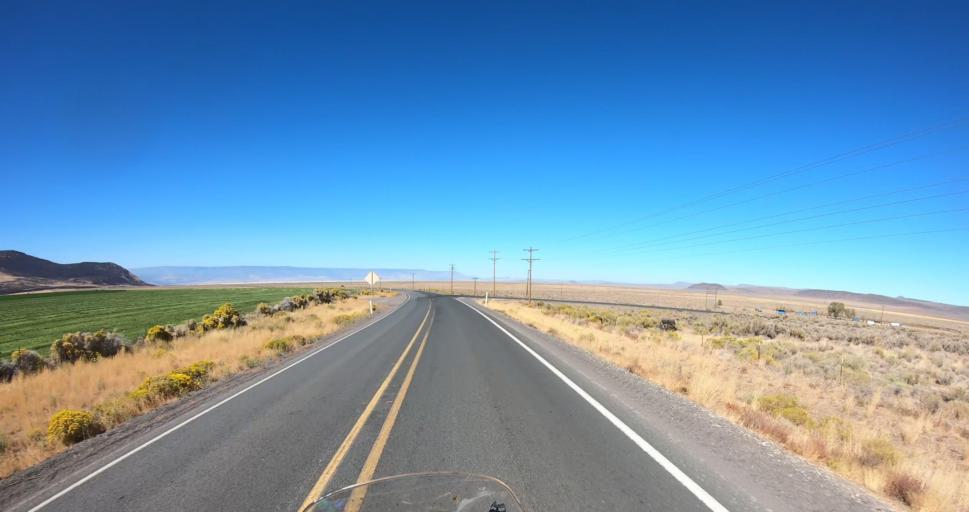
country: US
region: Oregon
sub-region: Lake County
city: Lakeview
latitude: 42.7037
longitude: -120.5481
